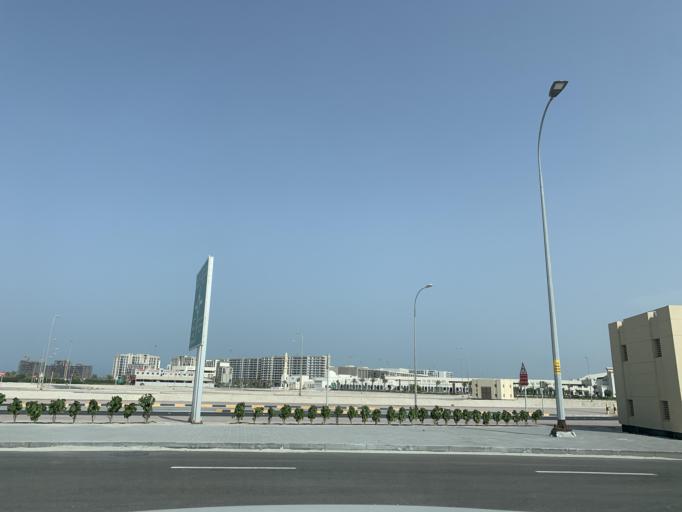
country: BH
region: Muharraq
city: Al Muharraq
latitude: 26.3075
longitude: 50.6345
